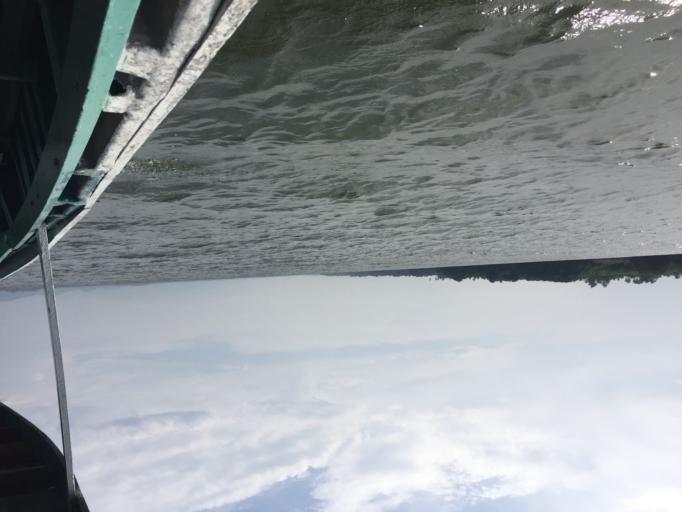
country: MX
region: Guerrero
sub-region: Coyuca de Benitez
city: Colonia Luces en el Mar
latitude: 16.9130
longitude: -99.9783
